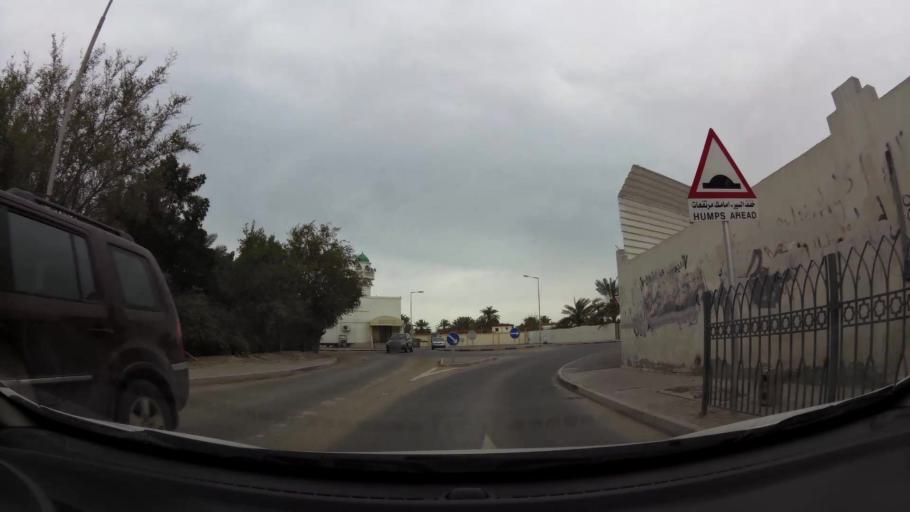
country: BH
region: Central Governorate
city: Madinat Hamad
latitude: 26.1438
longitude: 50.4579
